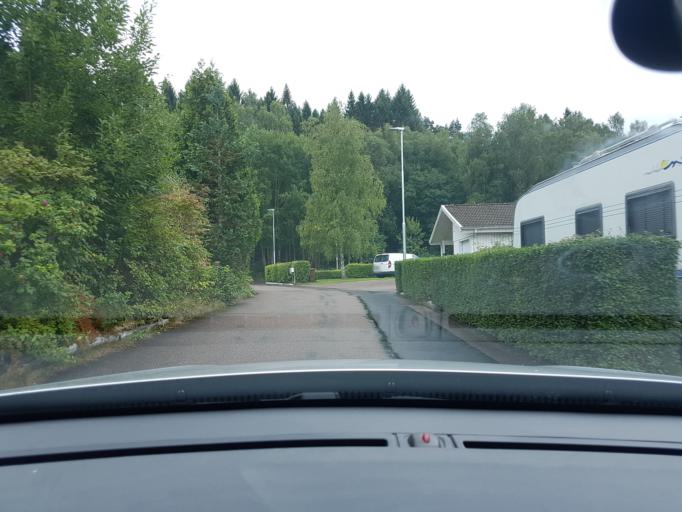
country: SE
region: Vaestra Goetaland
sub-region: Ale Kommun
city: Salanda
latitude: 57.9815
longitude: 12.2198
